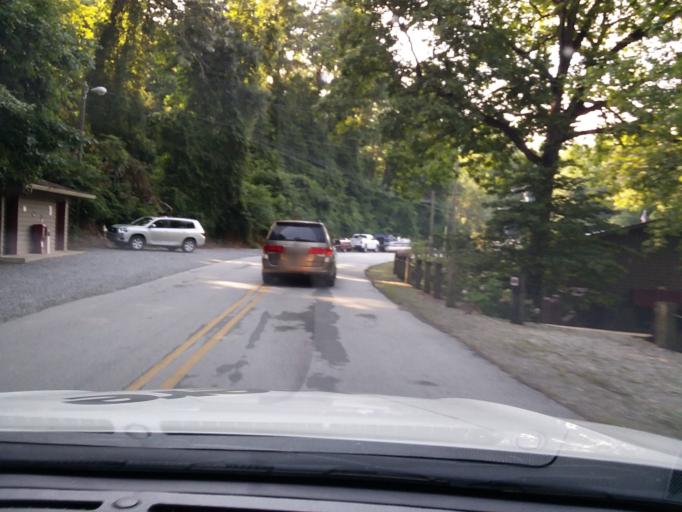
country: US
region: Georgia
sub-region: Rabun County
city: Clayton
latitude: 34.7696
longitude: -83.4354
